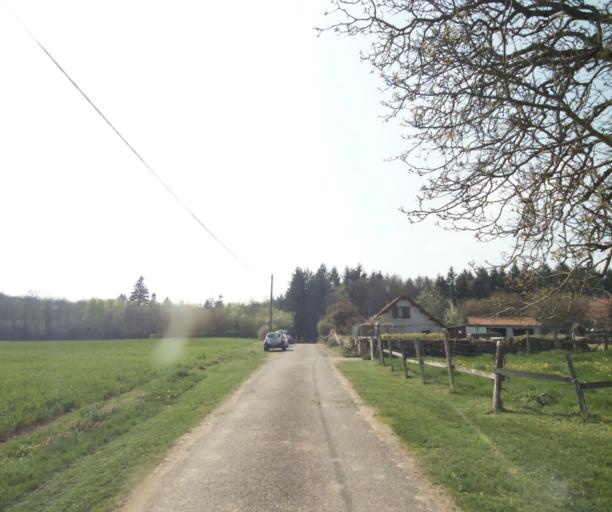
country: FR
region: Bourgogne
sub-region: Departement de Saone-et-Loire
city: Charolles
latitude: 46.4781
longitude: 4.4157
